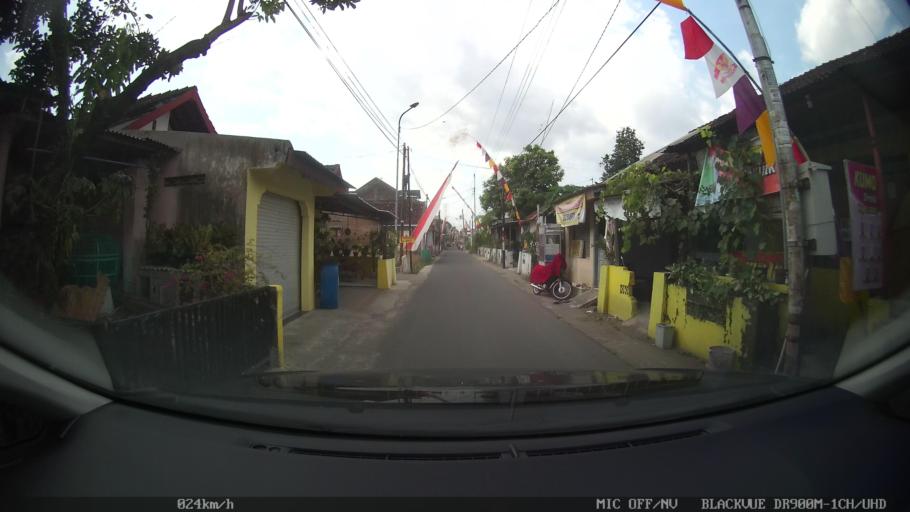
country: ID
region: Daerah Istimewa Yogyakarta
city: Gamping Lor
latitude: -7.8034
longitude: 110.3380
